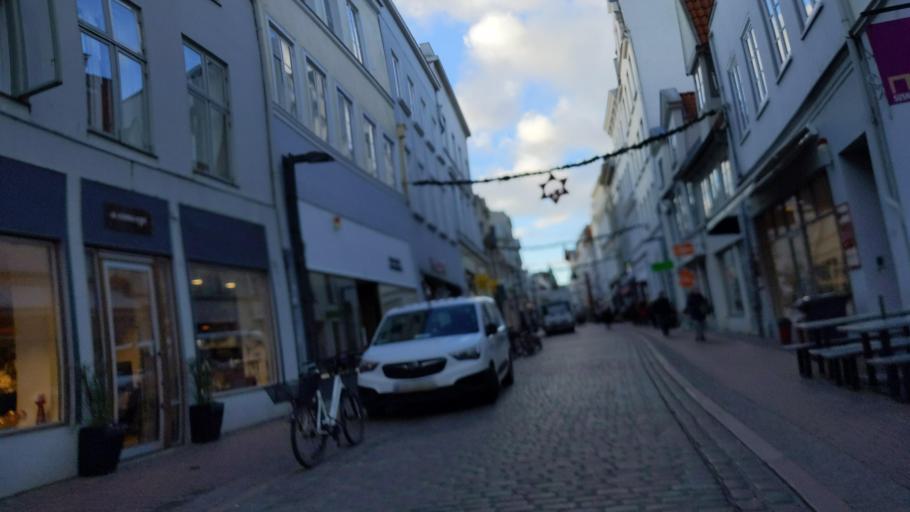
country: DE
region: Schleswig-Holstein
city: Luebeck
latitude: 53.8653
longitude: 10.6910
